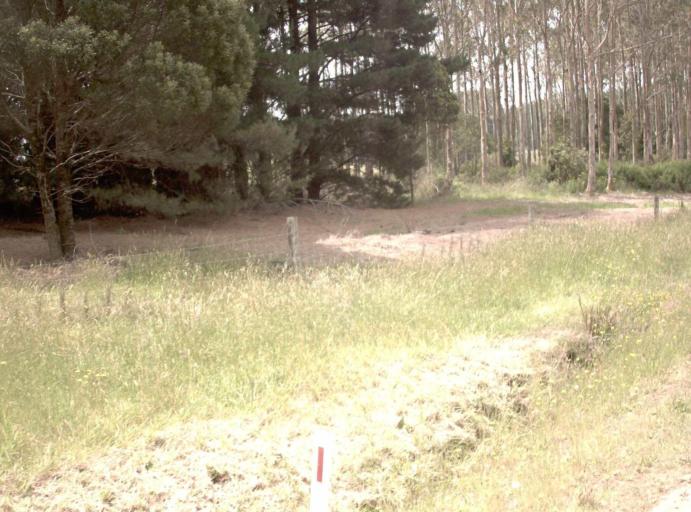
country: AU
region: Victoria
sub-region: Latrobe
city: Traralgon
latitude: -38.4052
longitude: 146.6402
